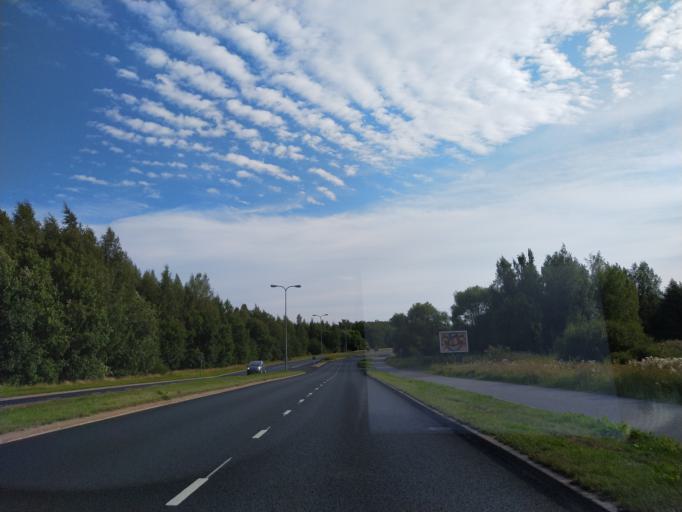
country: FI
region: Varsinais-Suomi
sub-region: Turku
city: Turku
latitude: 60.4260
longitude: 22.2396
